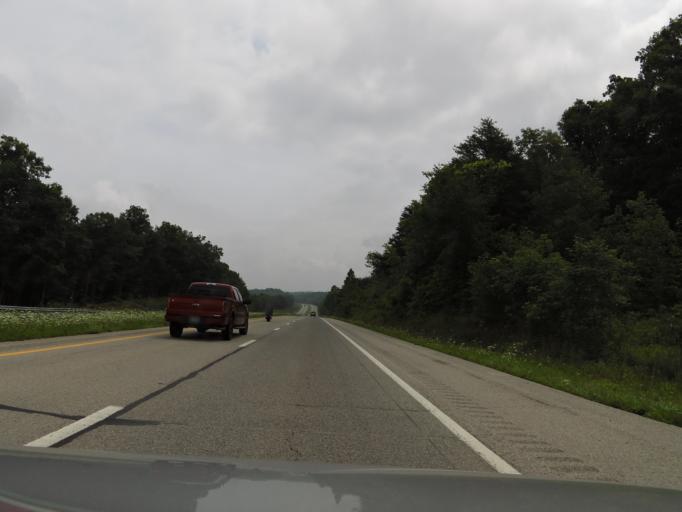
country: US
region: Kentucky
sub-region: Ohio County
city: Beaver Dam
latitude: 37.3339
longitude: -86.9574
